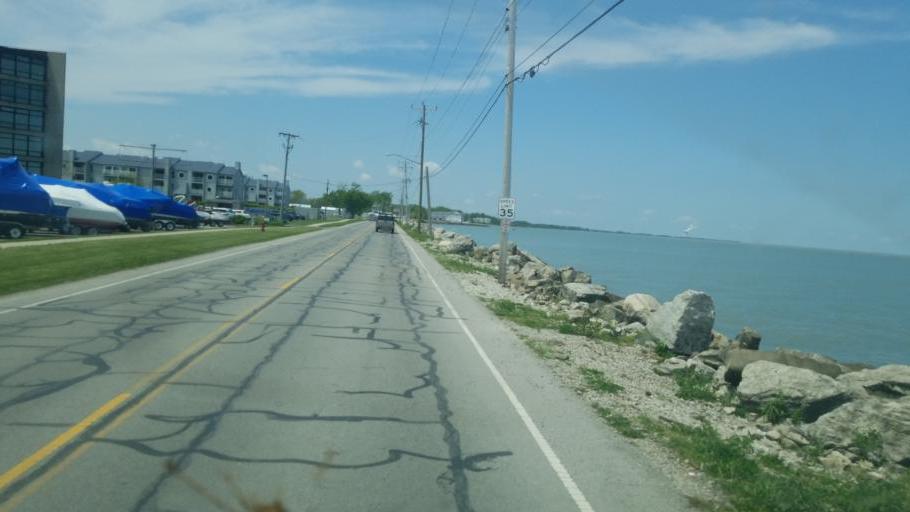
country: US
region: Ohio
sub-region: Ottawa County
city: Port Clinton
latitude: 41.5194
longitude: -82.9524
